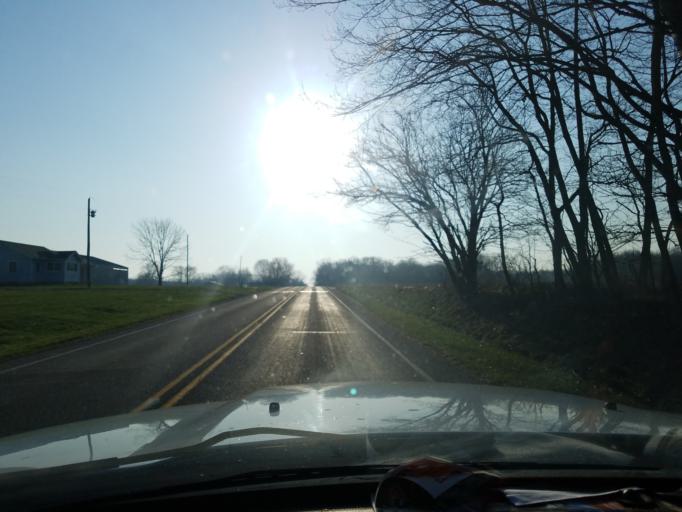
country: US
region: Indiana
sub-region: Clay County
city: Middlebury
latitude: 39.3883
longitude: -87.1758
